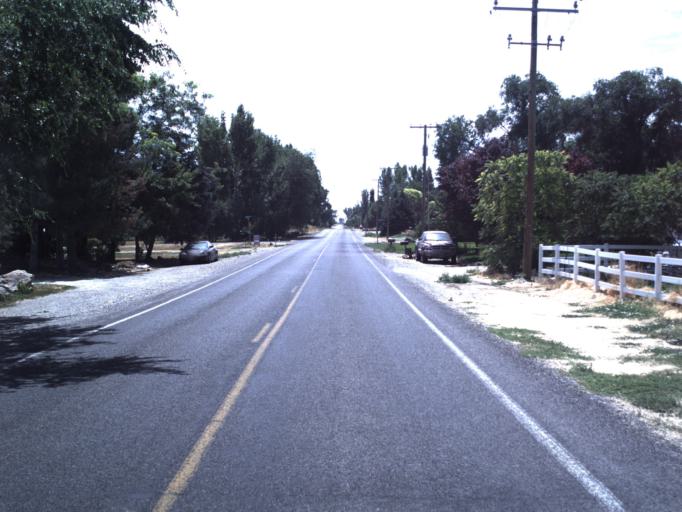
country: US
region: Utah
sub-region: Box Elder County
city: Tremonton
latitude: 41.6808
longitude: -112.2969
